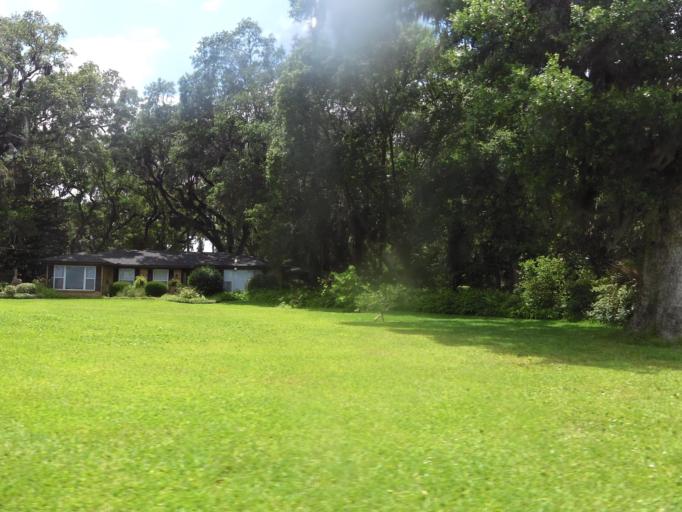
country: US
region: Florida
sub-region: Clay County
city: Orange Park
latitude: 30.1825
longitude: -81.6981
